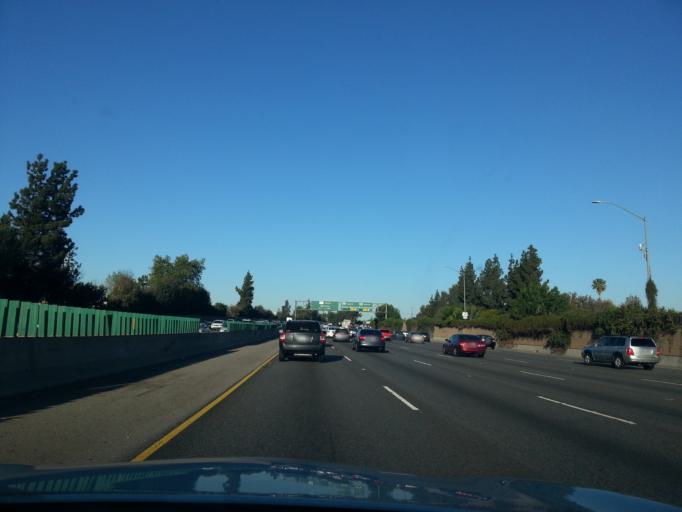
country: US
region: California
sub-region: Los Angeles County
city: Sherman Oaks
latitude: 34.1577
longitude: -118.4524
